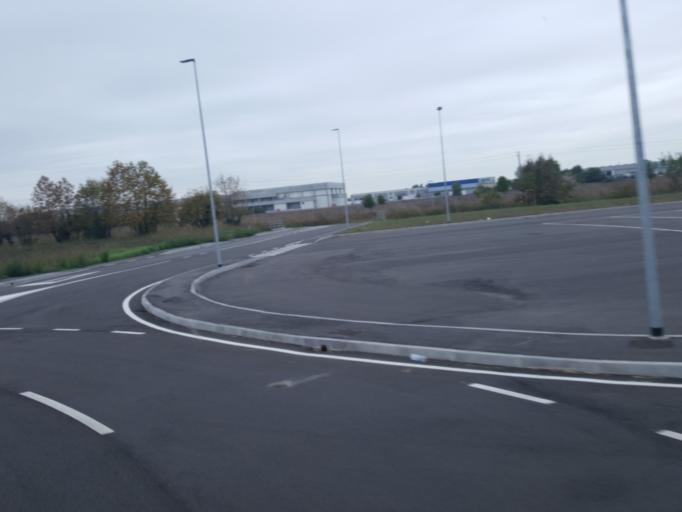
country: IT
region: Veneto
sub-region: Provincia di Verona
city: Pradelle
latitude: 45.2762
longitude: 10.8714
